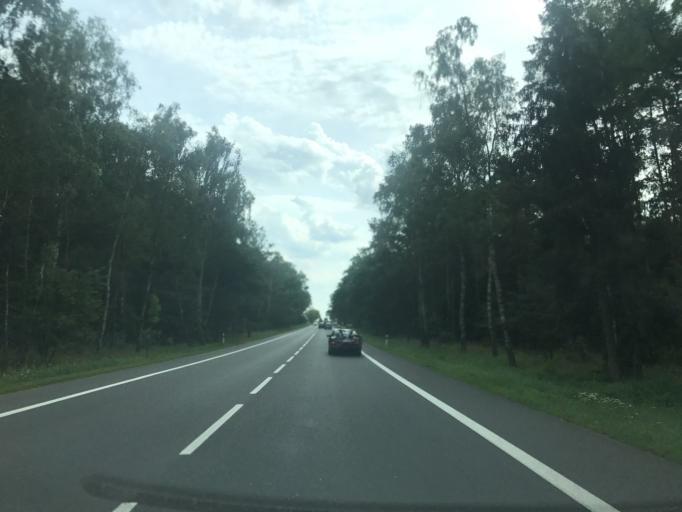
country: PL
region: Masovian Voivodeship
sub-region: Powiat mlawski
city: Strzegowo
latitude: 52.9093
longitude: 20.2868
